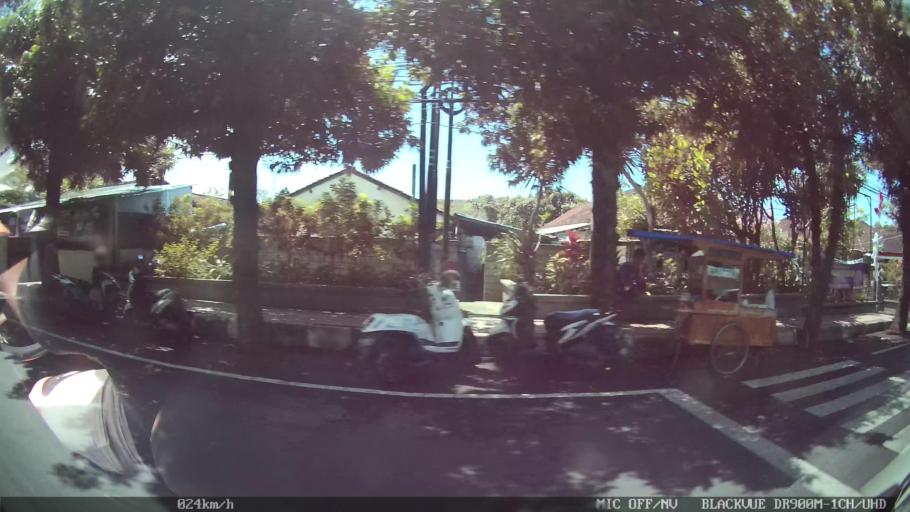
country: ID
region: Bali
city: Banjar Pasekan
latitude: -8.5947
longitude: 115.2828
